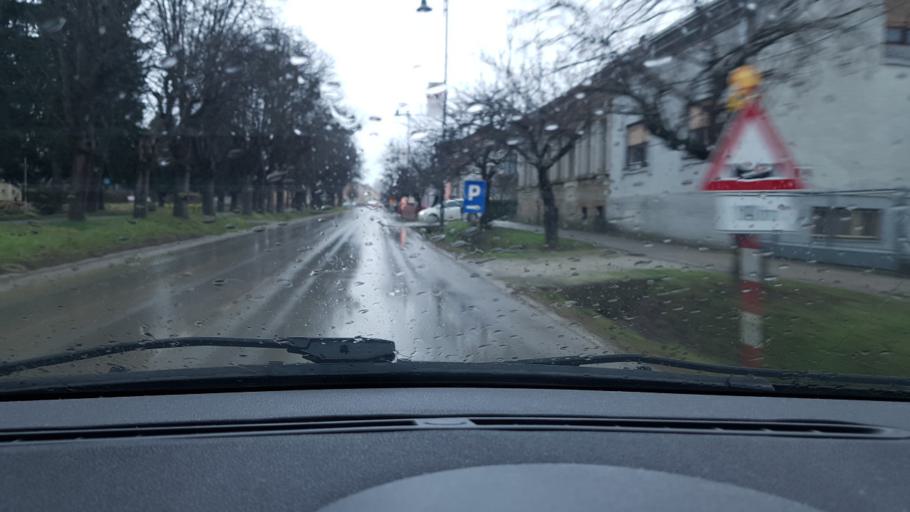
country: HR
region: Krapinsko-Zagorska
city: Oroslavje
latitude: 45.9810
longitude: 15.9647
